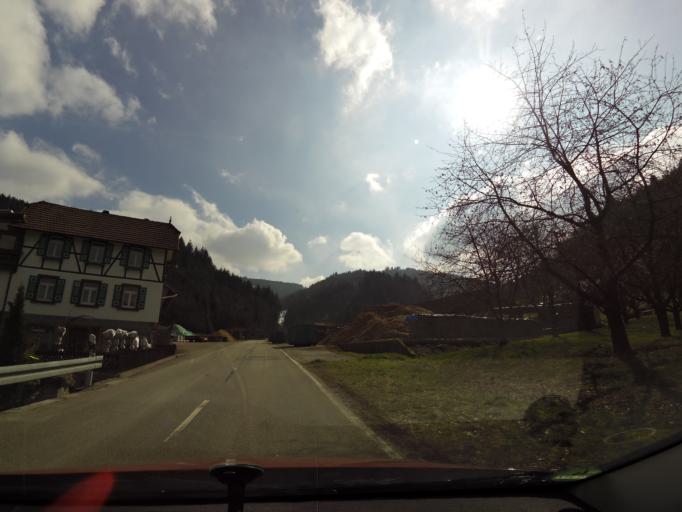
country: DE
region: Baden-Wuerttemberg
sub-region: Freiburg Region
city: Ottenhofen im Schwarzwald
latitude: 48.5546
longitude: 8.1560
